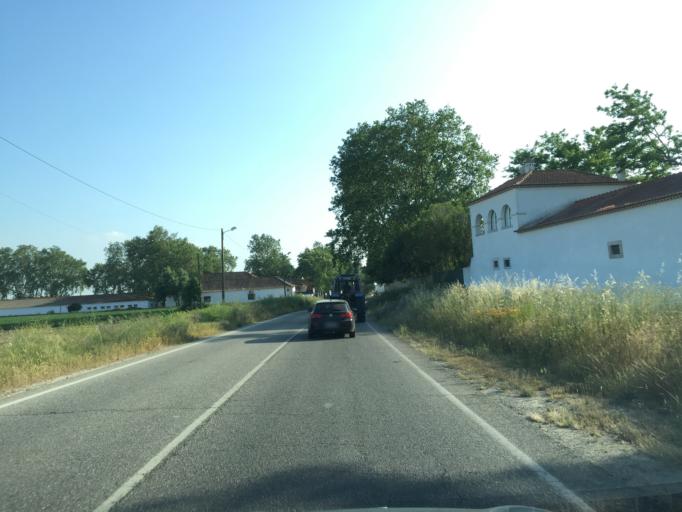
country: PT
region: Santarem
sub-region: Almeirim
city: Almeirim
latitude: 39.2011
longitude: -8.6381
